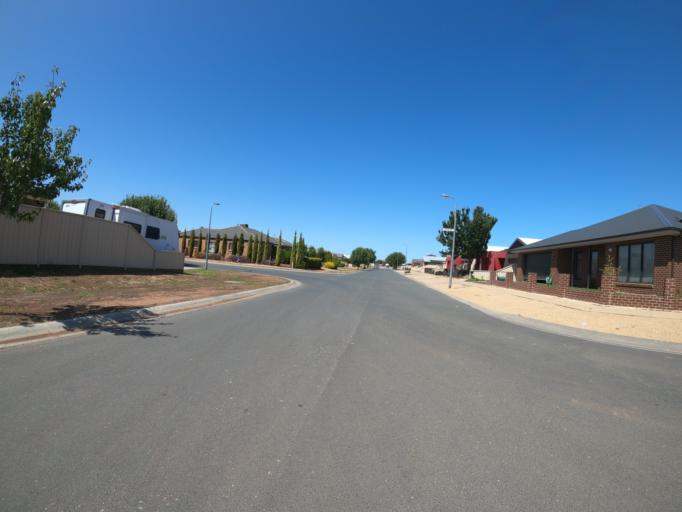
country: AU
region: Victoria
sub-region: Moira
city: Yarrawonga
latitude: -36.0106
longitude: 146.0254
